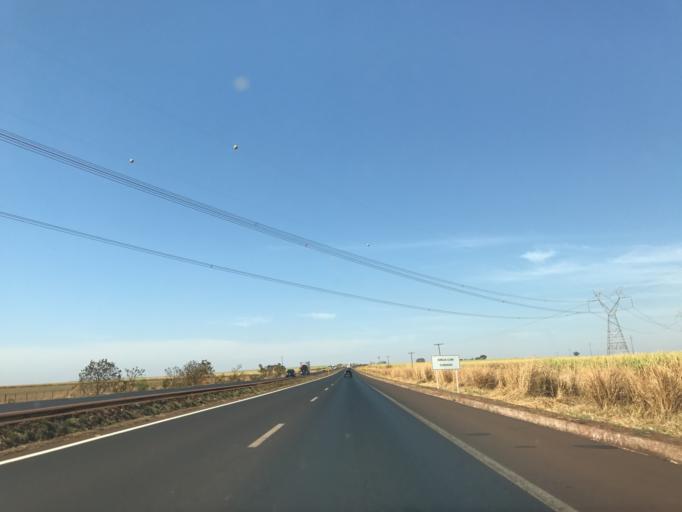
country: BR
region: Minas Gerais
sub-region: Centralina
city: Centralina
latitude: -18.5059
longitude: -49.1891
